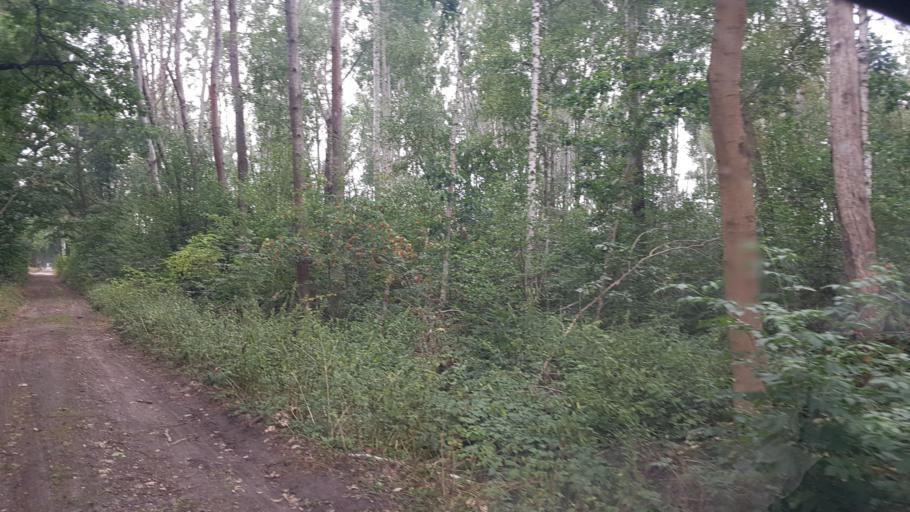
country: DE
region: Brandenburg
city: Bronkow
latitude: 51.6213
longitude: 13.9030
